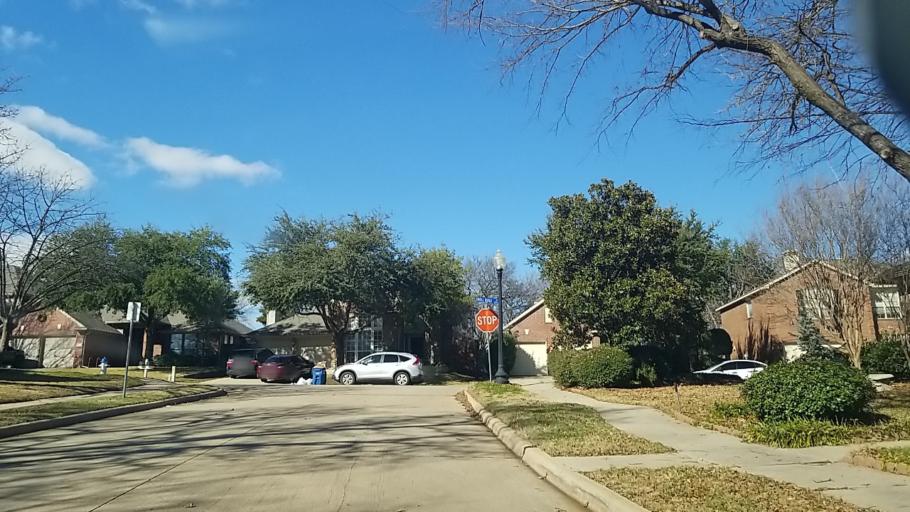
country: US
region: Texas
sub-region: Denton County
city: Corinth
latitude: 33.1589
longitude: -97.0747
